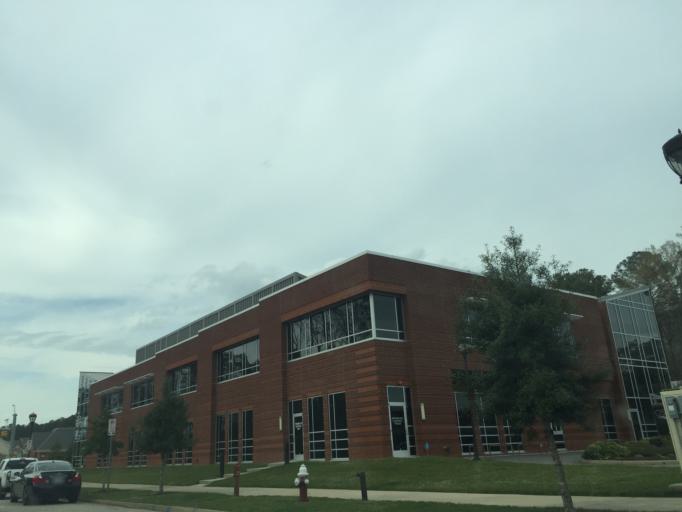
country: US
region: Virginia
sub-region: City of Newport News
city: Newport News
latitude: 37.0854
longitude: -76.4877
